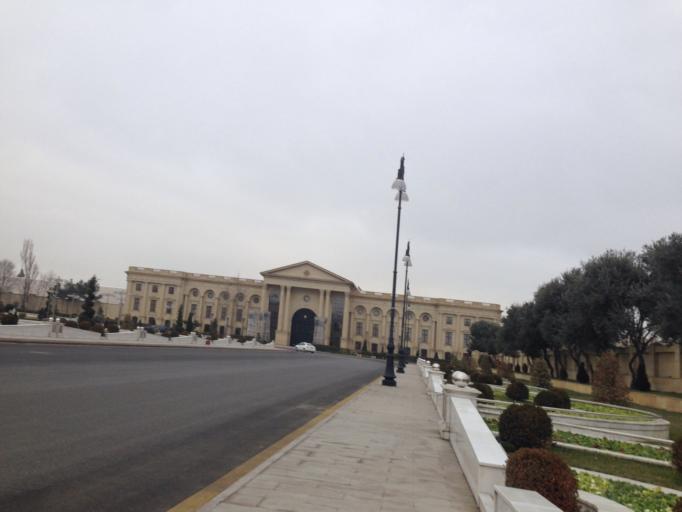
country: AZ
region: Baki
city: Baku
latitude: 40.4049
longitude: 49.8568
